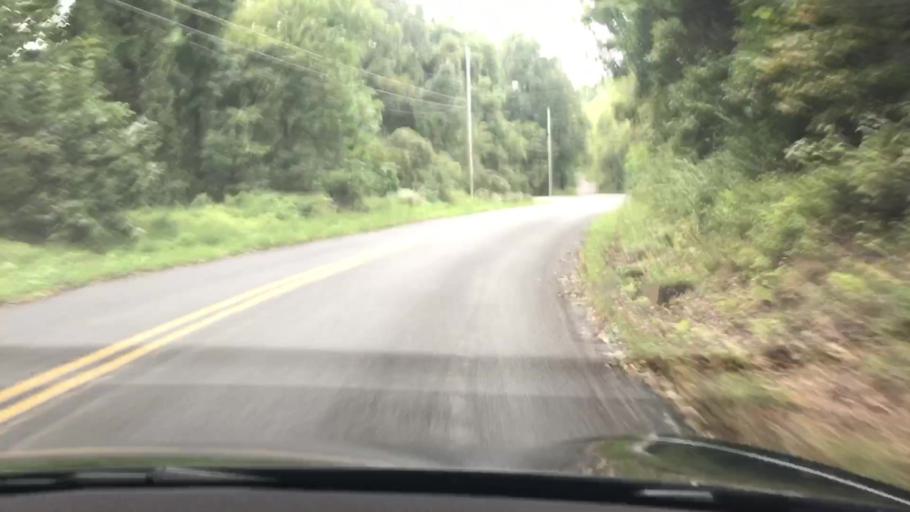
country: US
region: Pennsylvania
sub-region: York County
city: Dillsburg
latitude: 40.1112
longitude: -76.9717
